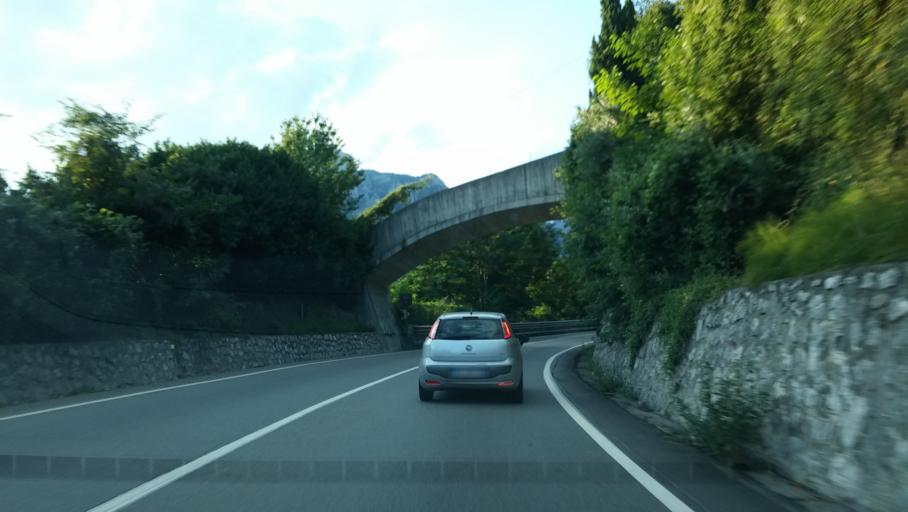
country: IT
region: Lombardy
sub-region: Provincia di Lecco
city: Lecco
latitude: 45.8607
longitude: 9.4152
